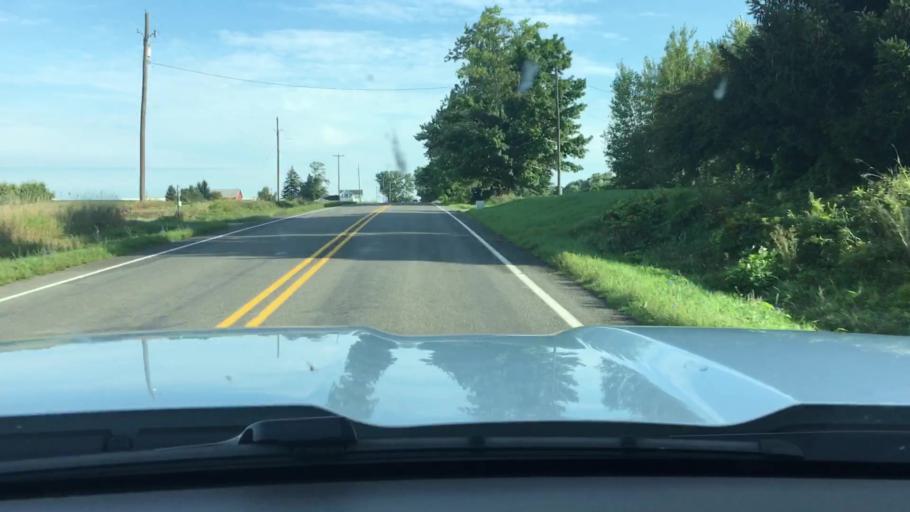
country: US
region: Michigan
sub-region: Kent County
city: Kent City
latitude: 43.1963
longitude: -85.7707
